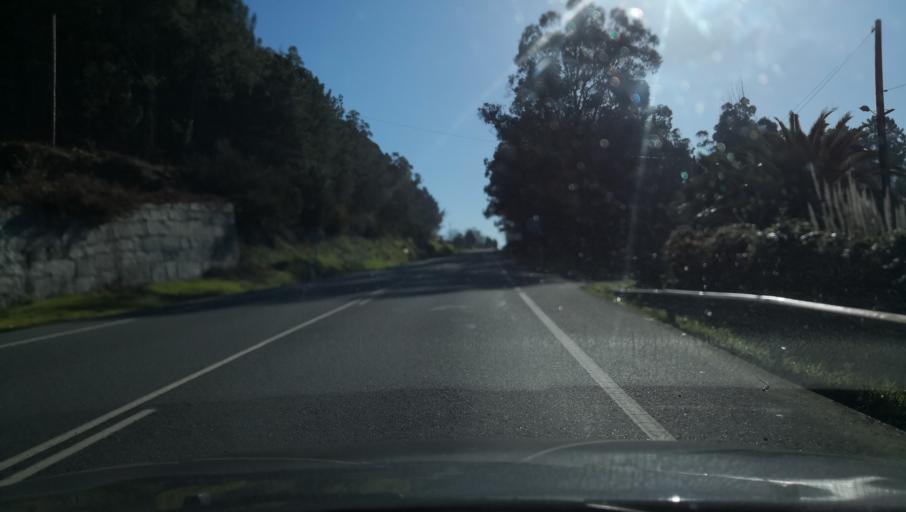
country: ES
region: Galicia
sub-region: Provincia da Coruna
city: Ribeira
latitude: 42.7561
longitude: -8.3907
